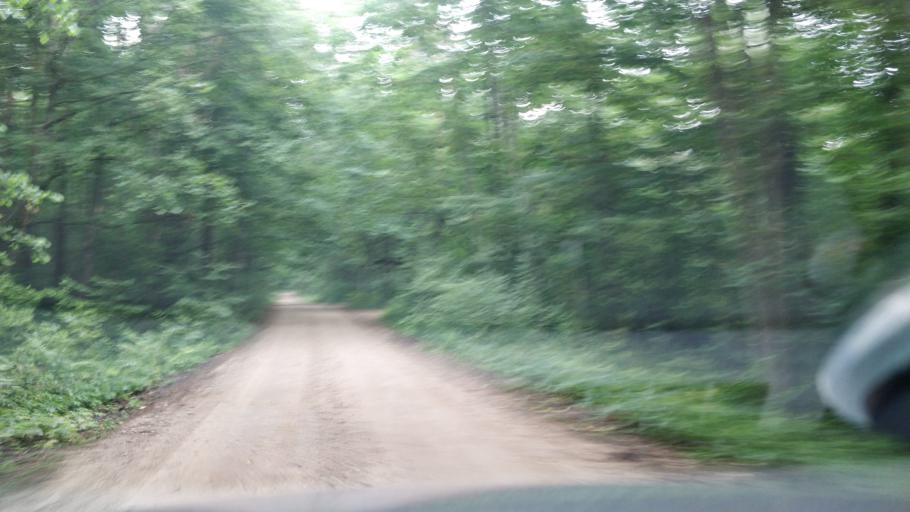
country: LV
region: Sigulda
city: Sigulda
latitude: 57.1508
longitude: 24.8310
